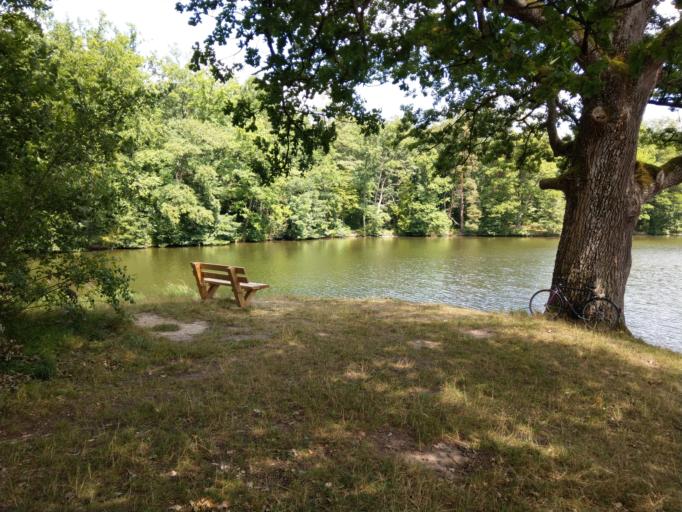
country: DE
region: Baden-Wuerttemberg
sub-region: Regierungsbezirk Stuttgart
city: Gerlingen
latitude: 48.7585
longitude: 9.1070
